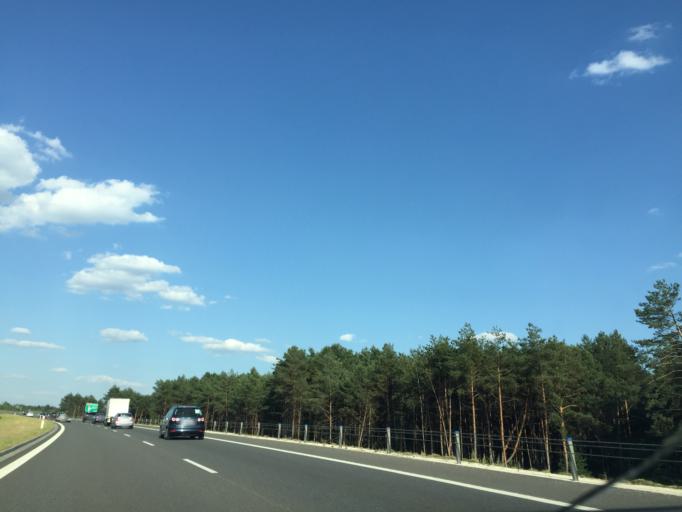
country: PL
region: Swietokrzyskie
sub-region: Powiat jedrzejowski
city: Sobkow
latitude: 50.7490
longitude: 20.4461
